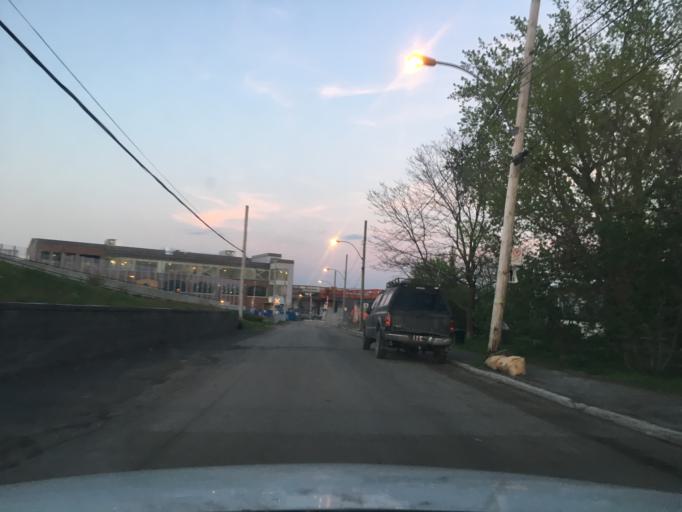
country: CA
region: Quebec
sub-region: Montreal
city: Montreal
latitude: 45.4819
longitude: -73.5550
